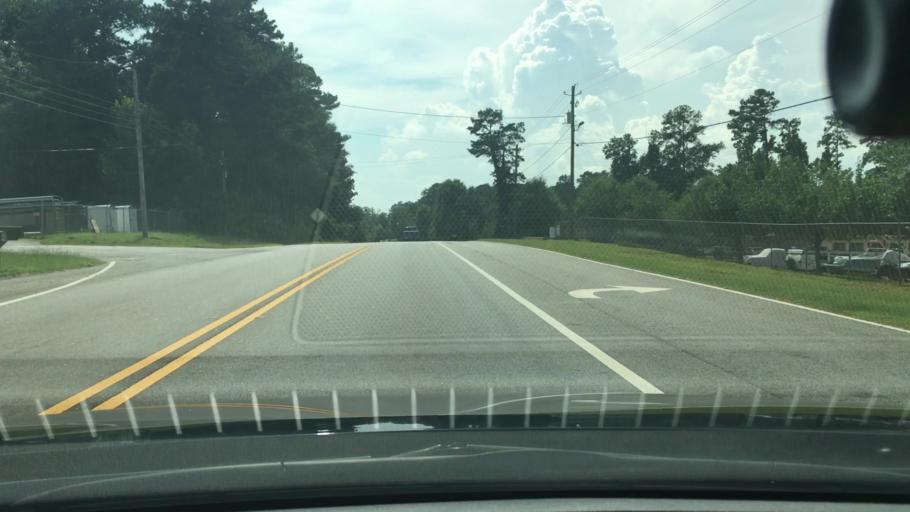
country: US
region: Georgia
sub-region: Coweta County
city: East Newnan
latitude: 33.3362
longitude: -84.7445
